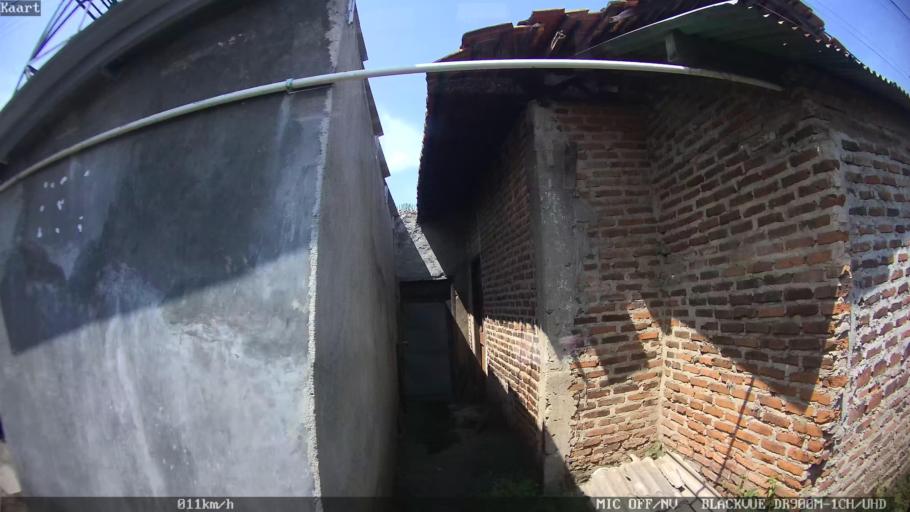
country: ID
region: Lampung
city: Kedaton
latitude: -5.3711
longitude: 105.2512
